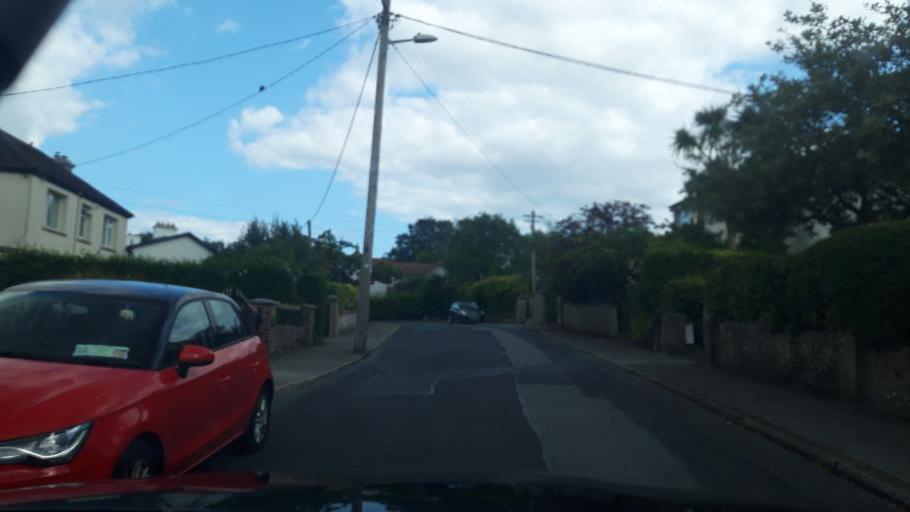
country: IE
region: Munster
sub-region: Waterford
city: Waterford
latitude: 52.2488
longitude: -7.0990
